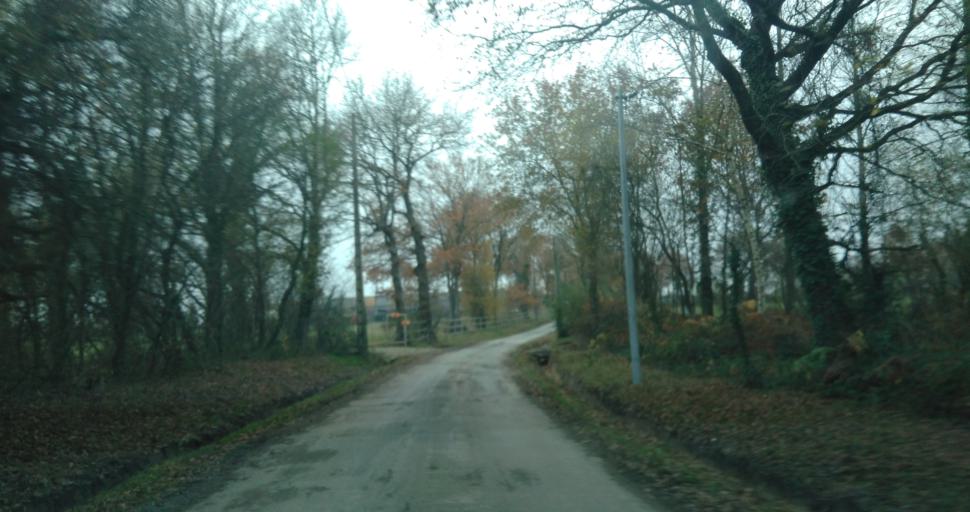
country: FR
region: Brittany
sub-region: Departement d'Ille-et-Vilaine
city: Iffendic
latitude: 48.1033
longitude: -2.0337
